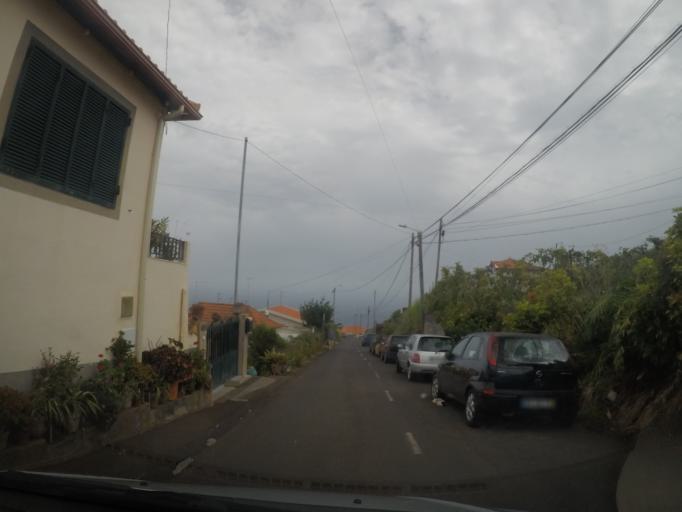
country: PT
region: Madeira
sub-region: Santa Cruz
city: Santa Cruz
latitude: 32.6841
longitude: -16.8094
